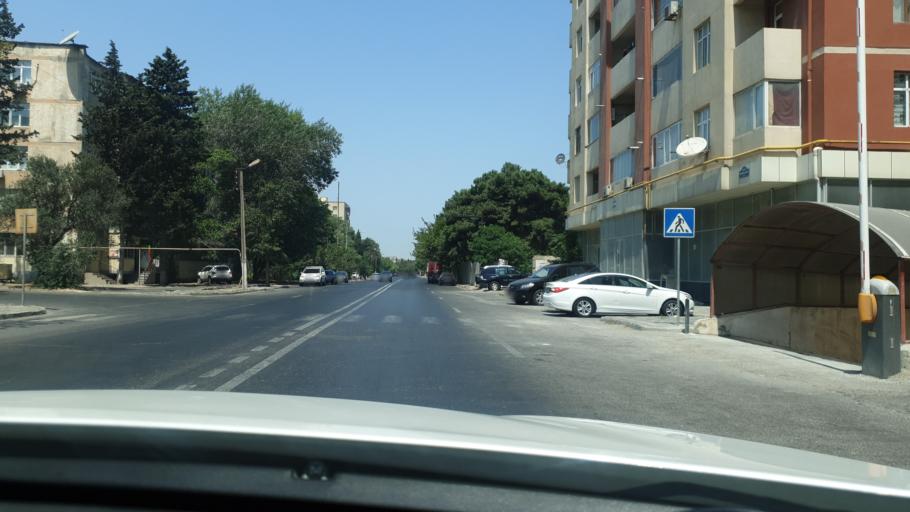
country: AZ
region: Baki
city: Bakixanov
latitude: 40.4149
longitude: 49.9481
